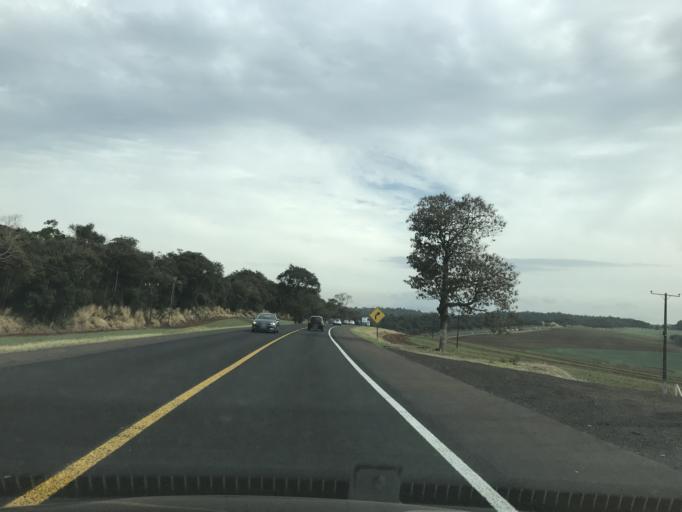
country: BR
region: Parana
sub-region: Matelandia
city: Matelandia
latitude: -25.1034
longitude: -53.7393
